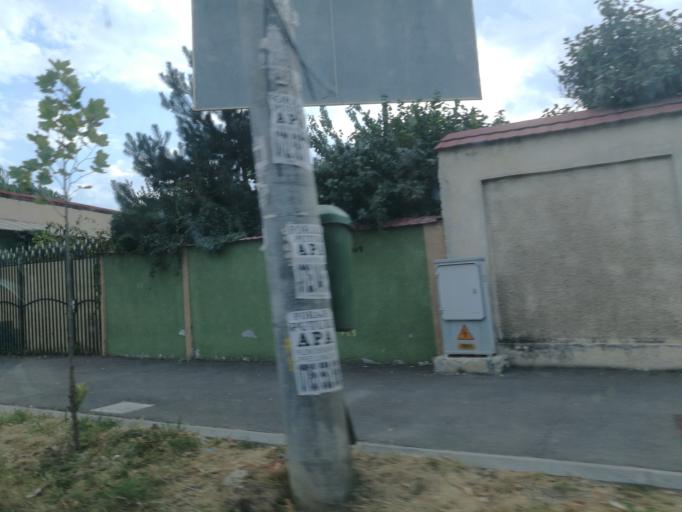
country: RO
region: Ilfov
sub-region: Comuna Mogosoaia
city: Mogosoaia
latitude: 44.5015
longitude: 26.0262
